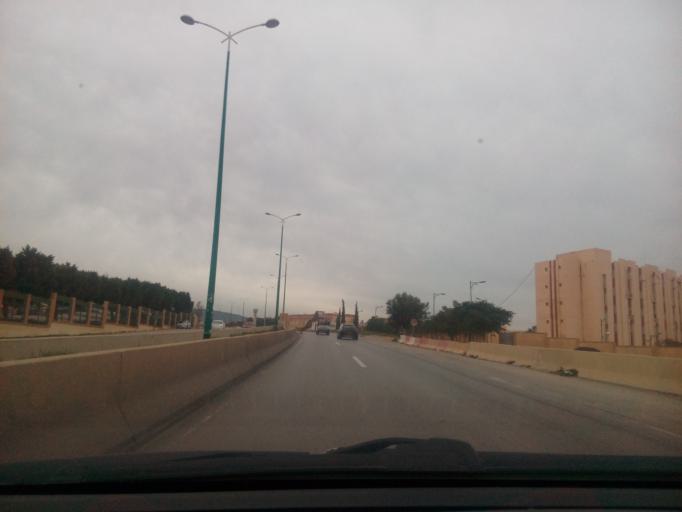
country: DZ
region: Tlemcen
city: Mansoura
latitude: 34.8982
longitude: -1.3545
